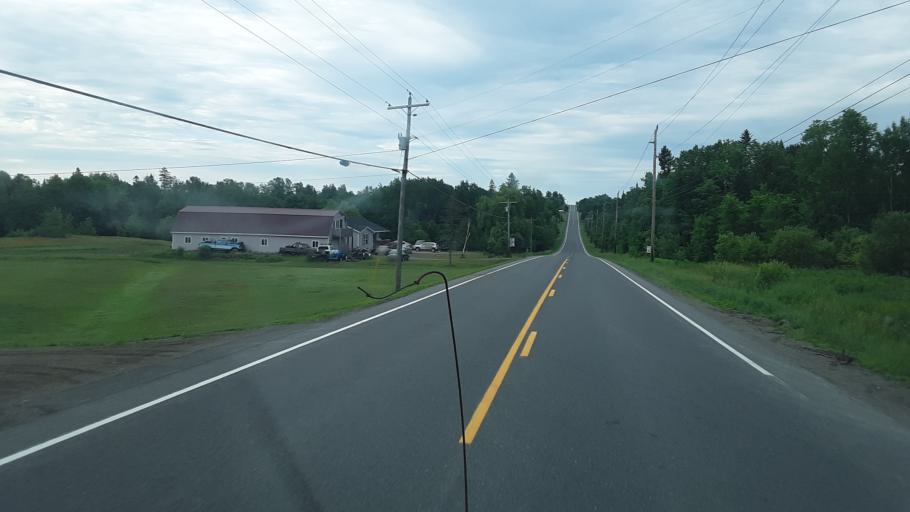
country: US
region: Maine
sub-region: Penobscot County
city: Patten
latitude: 45.9675
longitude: -68.4511
